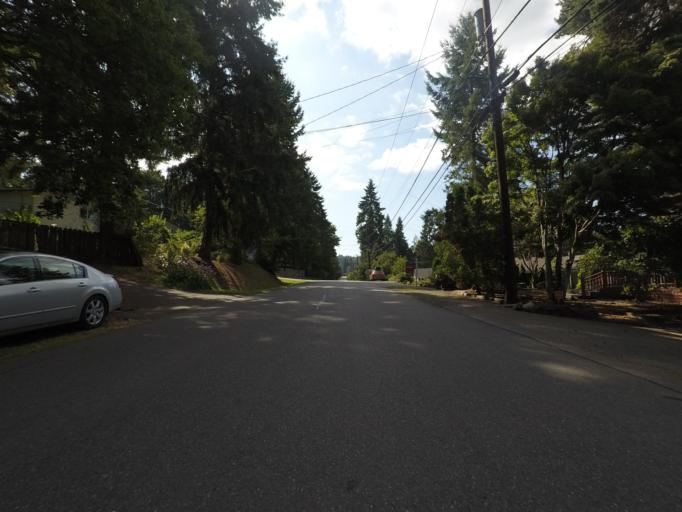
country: US
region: Washington
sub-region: King County
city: Kenmore
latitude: 47.7726
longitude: -122.2527
